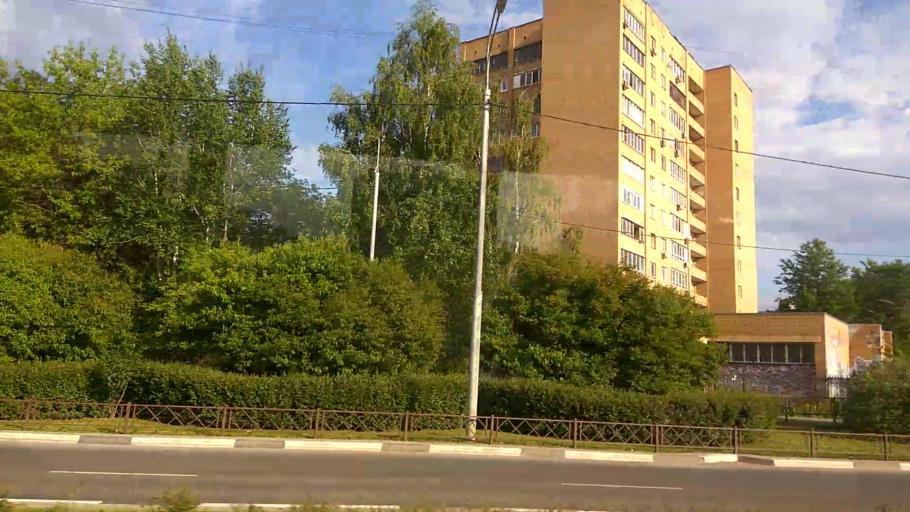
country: RU
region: Moskovskaya
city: Mytishchi
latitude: 55.9129
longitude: 37.7174
